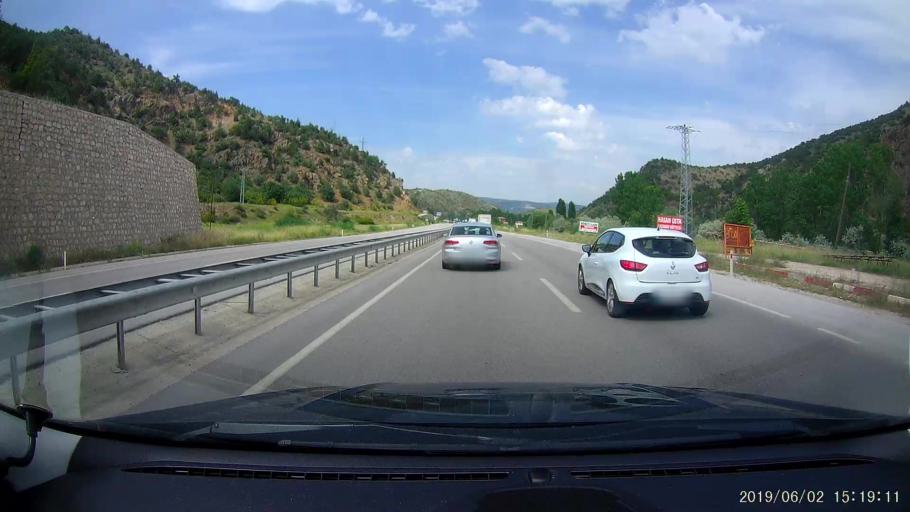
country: TR
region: Corum
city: Osmancik
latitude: 40.9681
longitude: 34.9063
